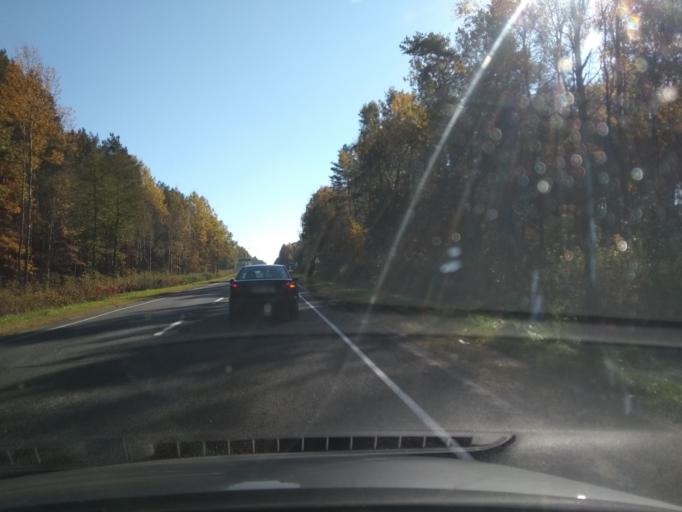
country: BY
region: Brest
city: Malaryta
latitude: 51.8942
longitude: 24.1357
